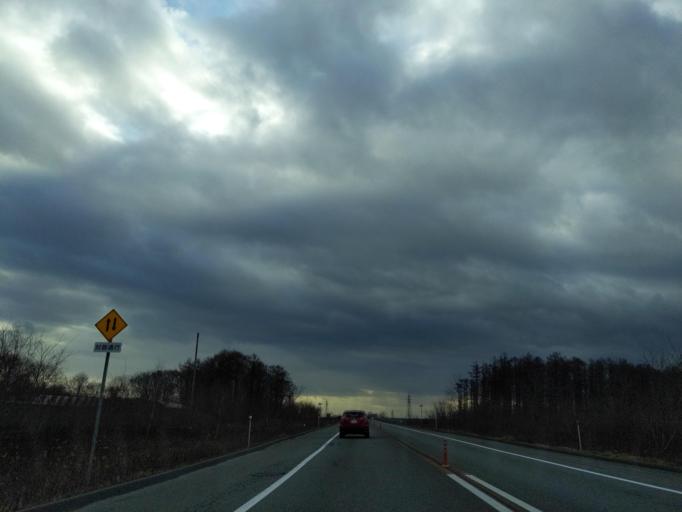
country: JP
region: Hokkaido
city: Chitose
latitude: 42.8449
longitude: 141.6967
